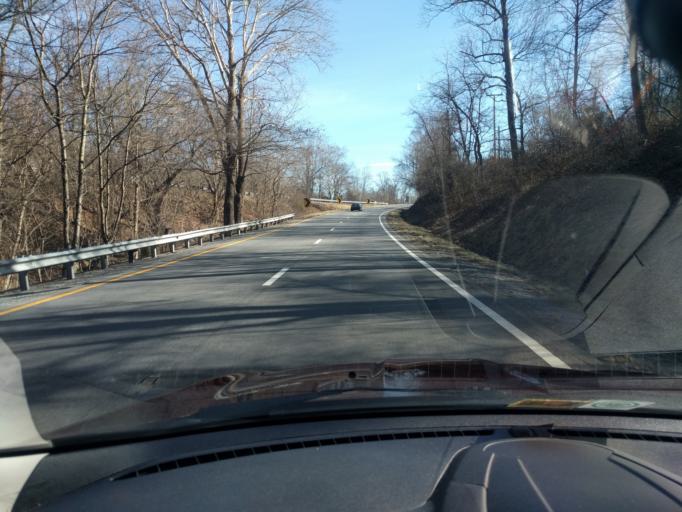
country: US
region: Virginia
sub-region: Botetourt County
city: Blue Ridge
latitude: 37.3635
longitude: -79.6867
